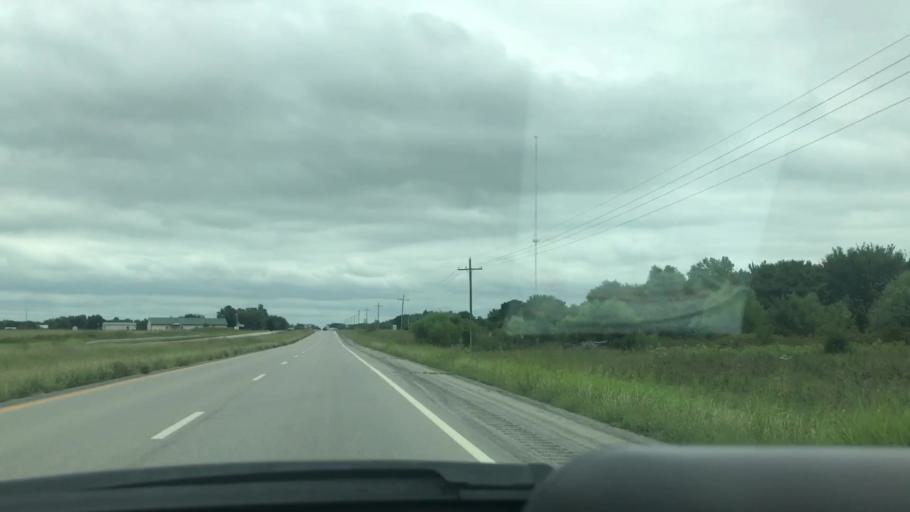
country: US
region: Oklahoma
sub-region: Mayes County
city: Pryor
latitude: 36.4196
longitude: -95.2779
